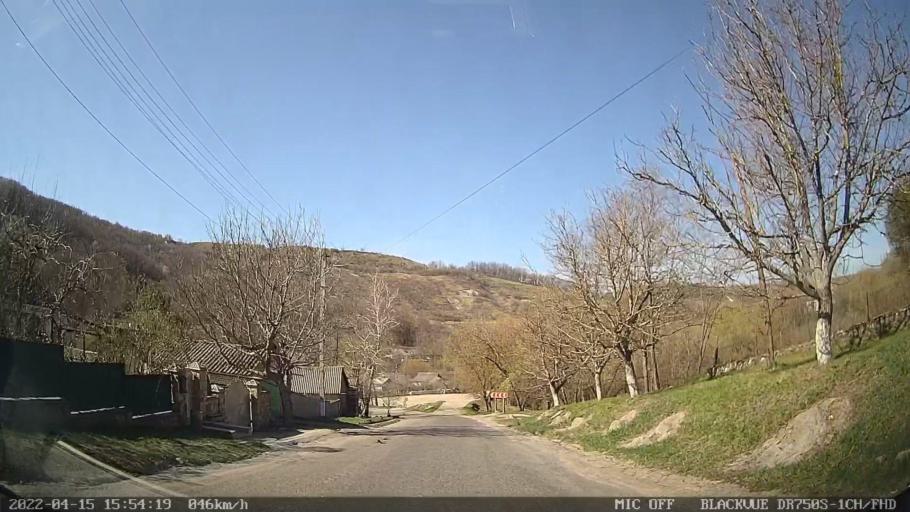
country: MD
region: Raionul Ocnita
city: Otaci
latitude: 48.4031
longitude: 27.8905
